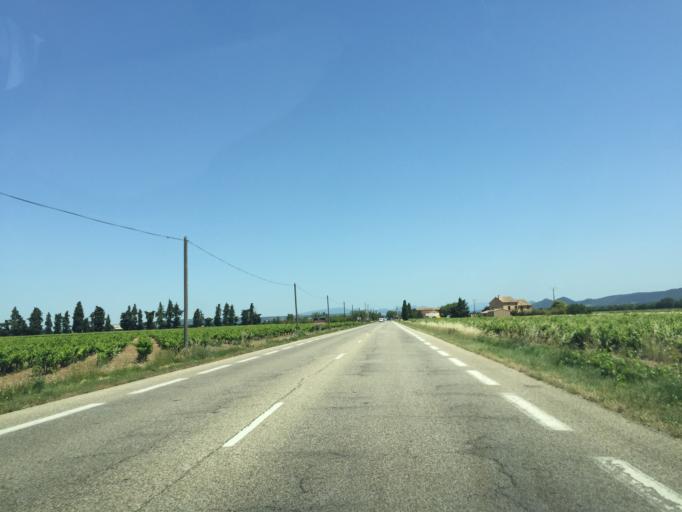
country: FR
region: Provence-Alpes-Cote d'Azur
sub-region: Departement du Vaucluse
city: Violes
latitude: 44.1315
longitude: 4.9343
